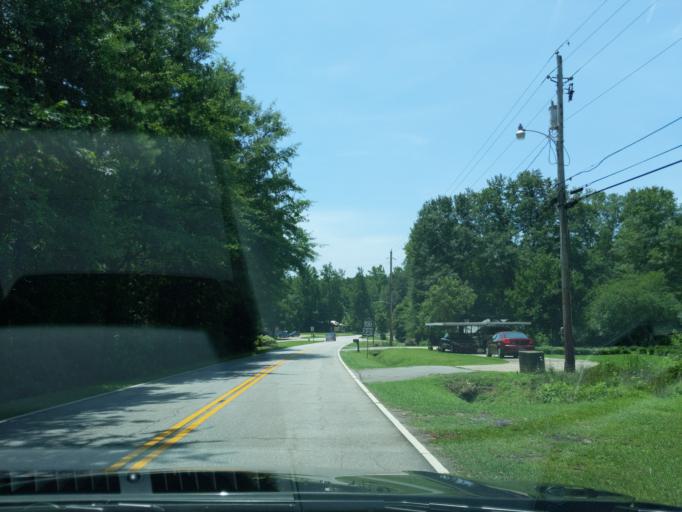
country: US
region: South Carolina
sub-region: Laurens County
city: Laurens
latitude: 34.4778
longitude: -82.0271
